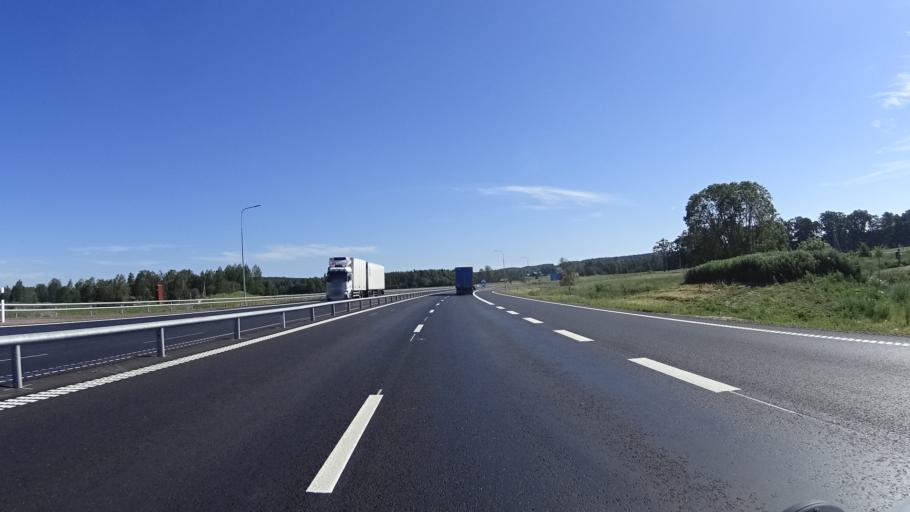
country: SE
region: Vaestra Goetaland
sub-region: Gullspangs Kommun
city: Hova
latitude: 58.8625
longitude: 14.2190
